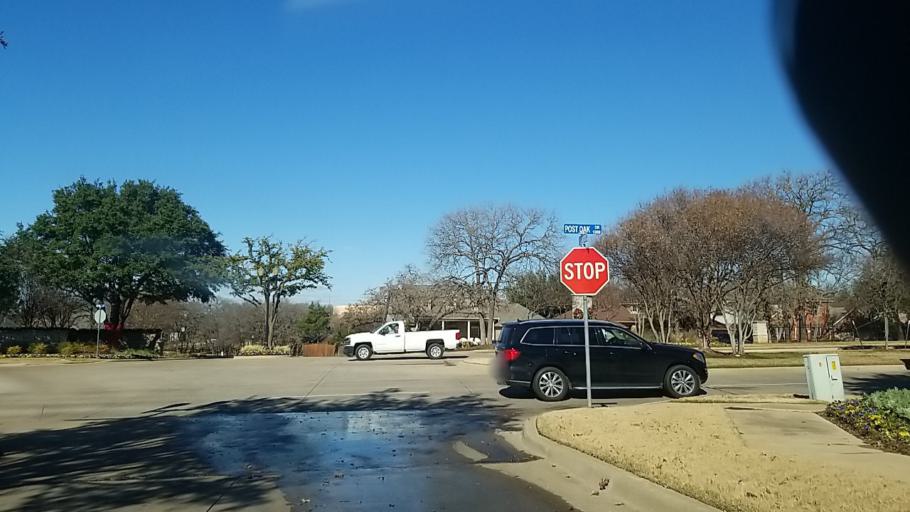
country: US
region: Texas
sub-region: Denton County
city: Corinth
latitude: 33.1592
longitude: -97.0769
